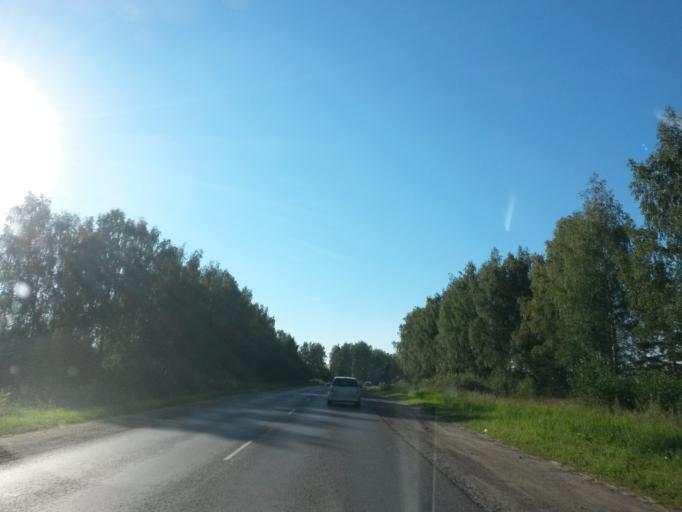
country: RU
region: Ivanovo
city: Novo-Talitsy
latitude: 57.0249
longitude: 40.7617
